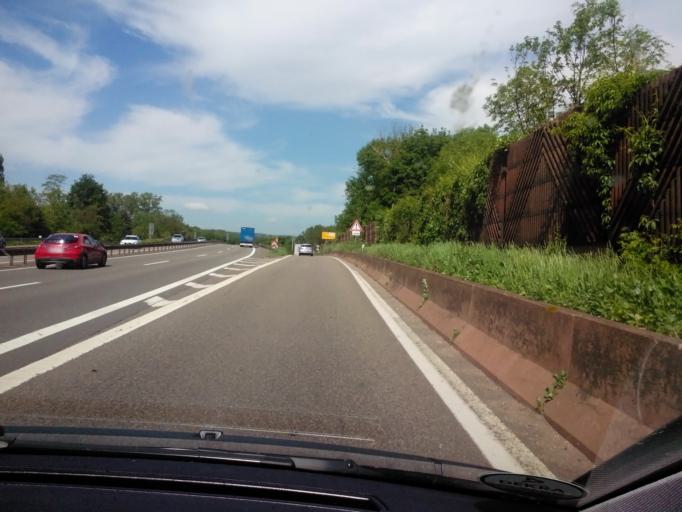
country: DE
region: Saarland
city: Saarlouis
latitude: 49.3040
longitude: 6.7426
